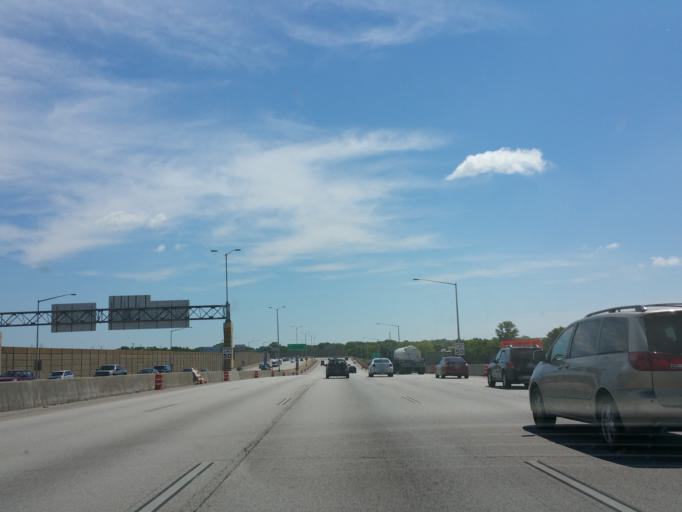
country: US
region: Wisconsin
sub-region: Milwaukee County
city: Saint Francis
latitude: 42.9661
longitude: -87.9262
